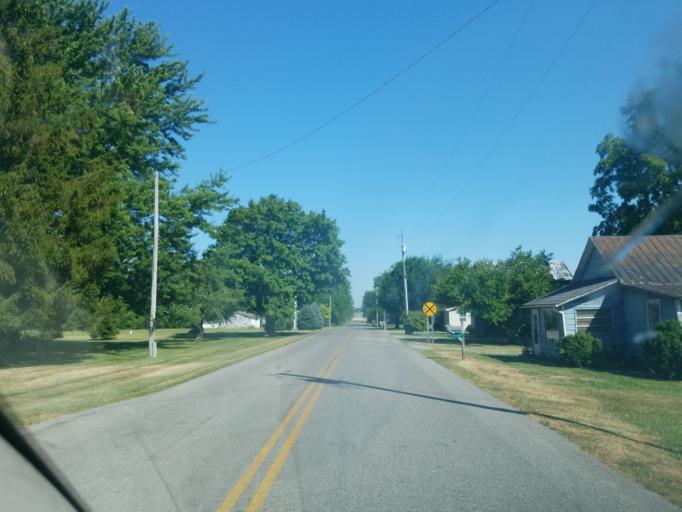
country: US
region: Ohio
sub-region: Logan County
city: Northwood
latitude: 40.4286
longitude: -83.7077
